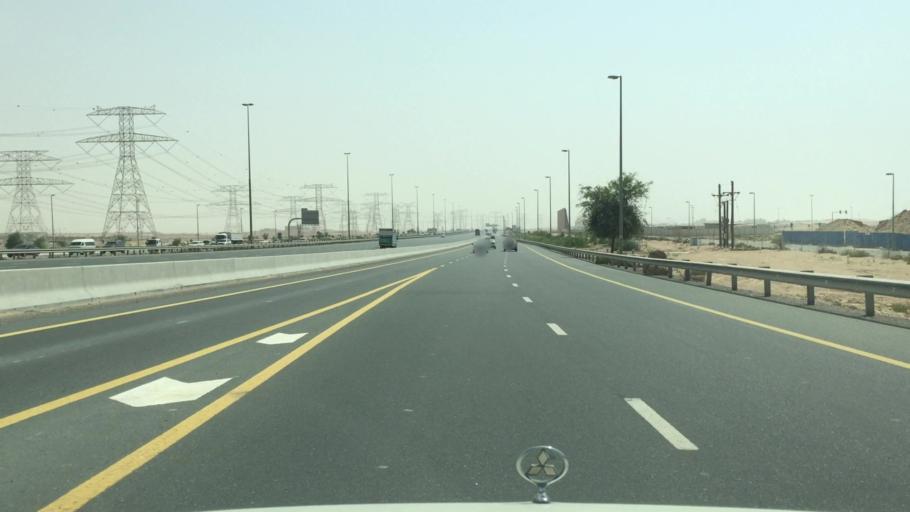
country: AE
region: Dubai
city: Dubai
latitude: 25.0851
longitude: 55.3883
